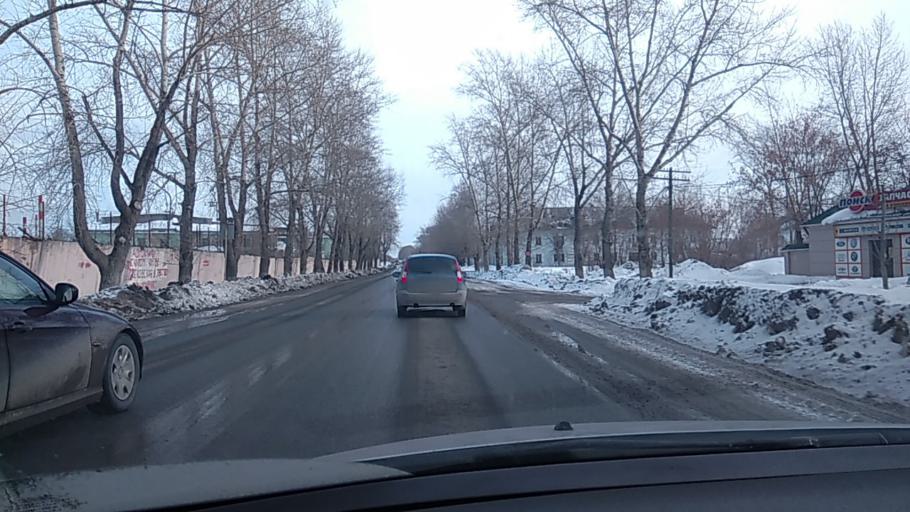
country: RU
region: Sverdlovsk
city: Martyush
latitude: 56.4473
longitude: 61.8138
